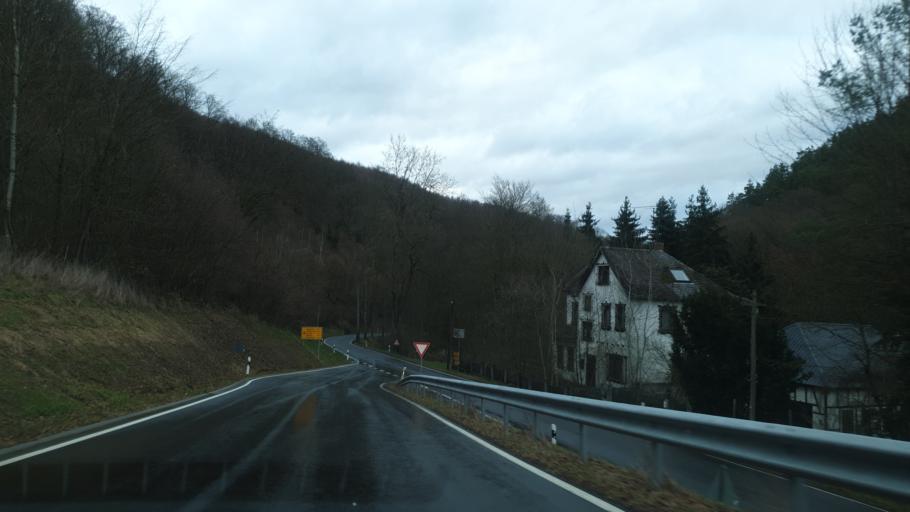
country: DE
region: Rheinland-Pfalz
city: Biebrich
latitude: 50.3095
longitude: 7.9381
